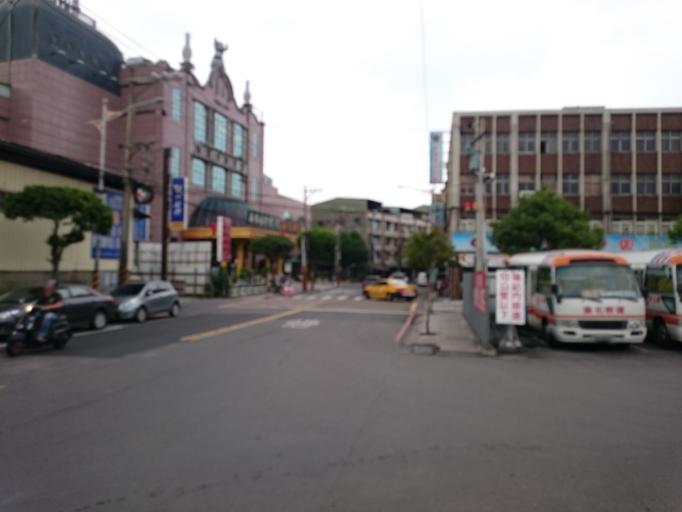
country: TW
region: Taipei
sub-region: Taipei
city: Banqiao
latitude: 24.9902
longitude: 121.4909
